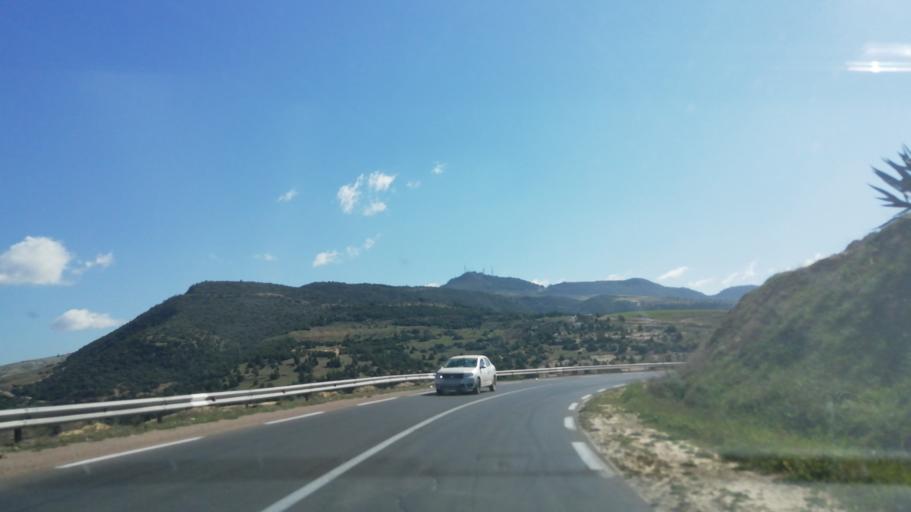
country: DZ
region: Mascara
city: Mascara
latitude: 35.4931
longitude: 0.1369
